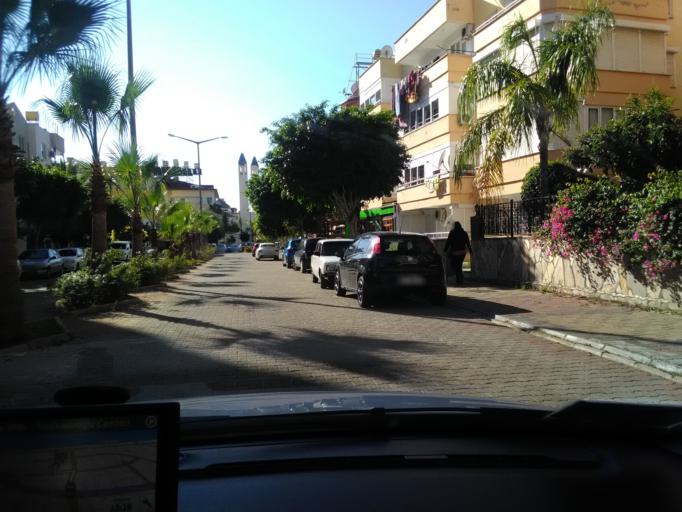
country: TR
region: Antalya
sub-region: Alanya
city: Alanya
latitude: 36.5359
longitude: 32.0433
